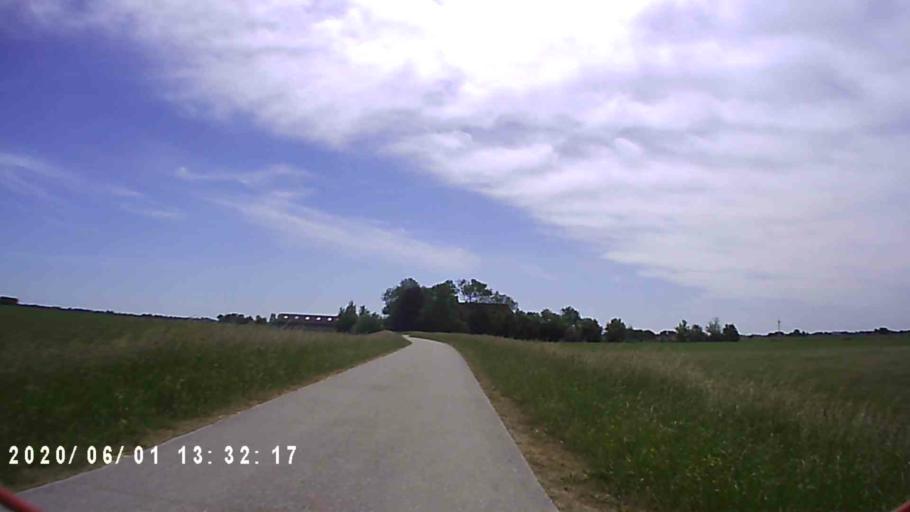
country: NL
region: Friesland
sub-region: Gemeente Littenseradiel
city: Wommels
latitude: 53.0935
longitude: 5.5678
